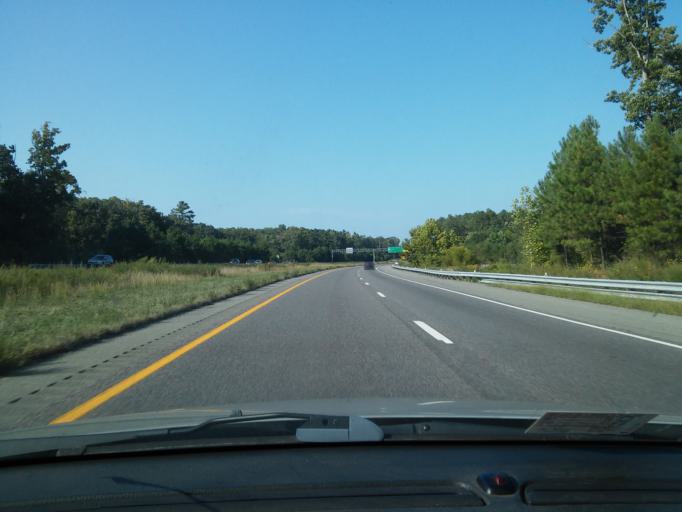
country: US
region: Virginia
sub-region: Henrico County
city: Short Pump
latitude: 37.6026
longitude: -77.6665
